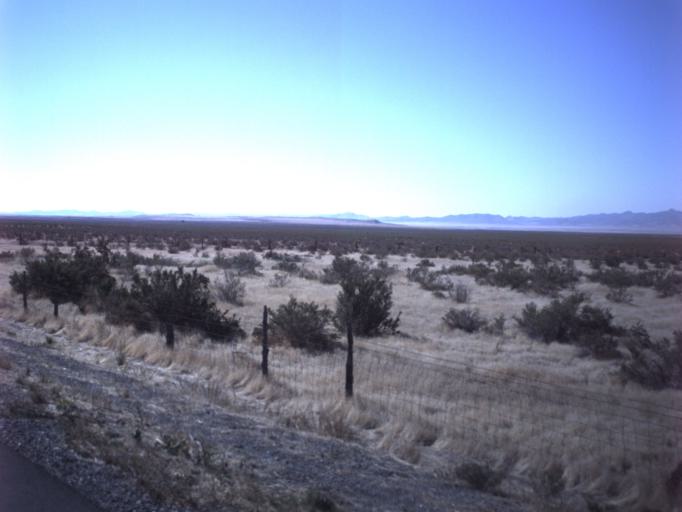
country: US
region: Utah
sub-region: Tooele County
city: Grantsville
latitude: 40.4855
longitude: -112.7459
